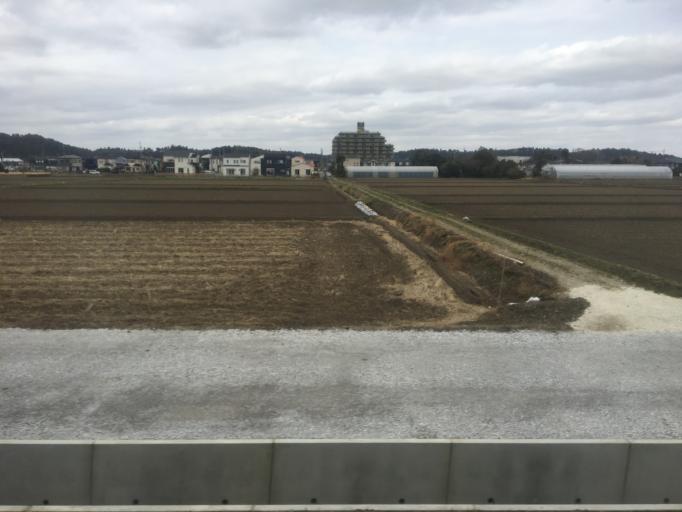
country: JP
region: Chiba
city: Togane
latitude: 35.5721
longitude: 140.3872
